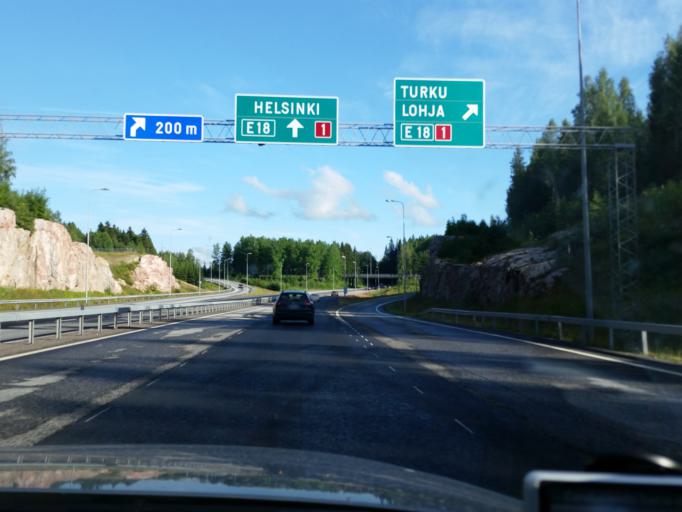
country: FI
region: Uusimaa
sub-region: Helsinki
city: Vihti
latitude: 60.2963
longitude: 24.3631
